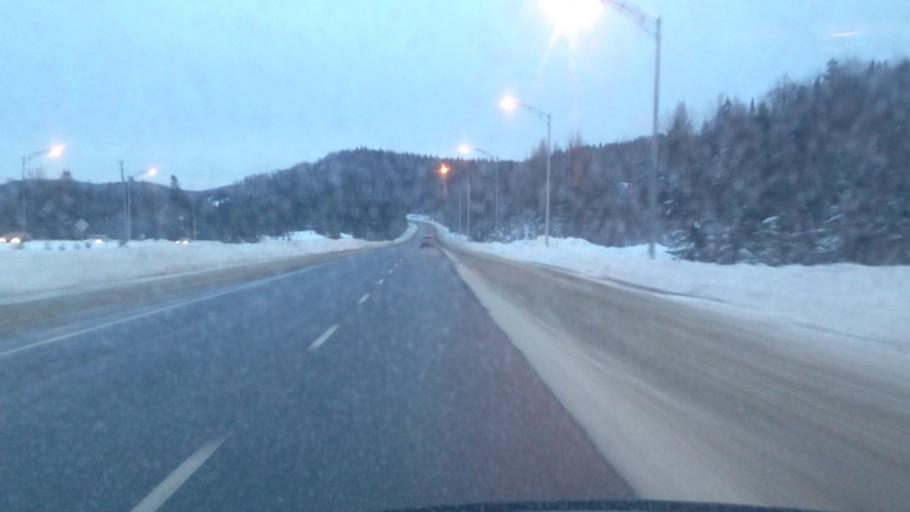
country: CA
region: Quebec
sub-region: Laurentides
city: Sainte-Agathe-des-Monts
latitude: 46.1180
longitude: -74.4315
